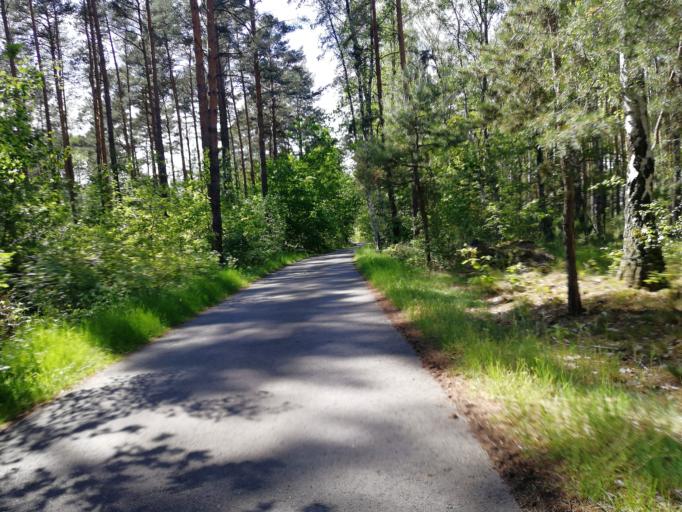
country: DE
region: Brandenburg
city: Calau
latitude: 51.7227
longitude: 13.9262
